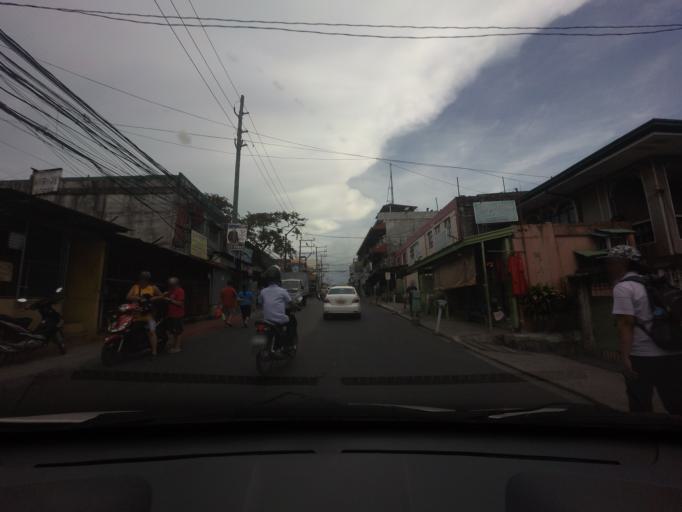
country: PH
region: Calabarzon
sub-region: Province of Rizal
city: Taguig
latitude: 14.5079
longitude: 121.0536
